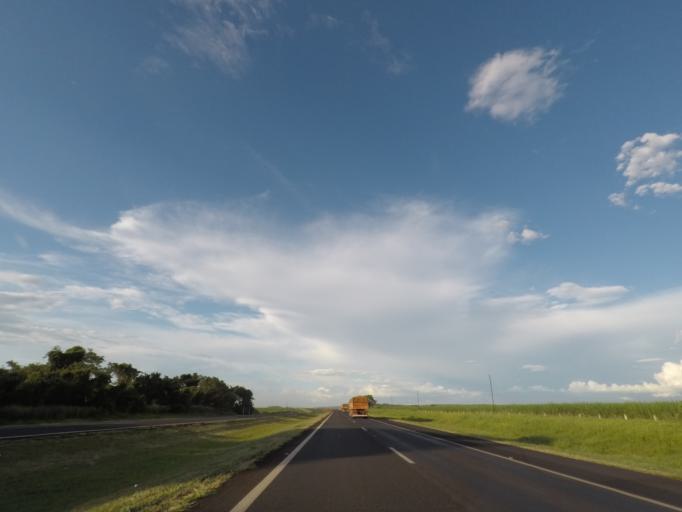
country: BR
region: Sao Paulo
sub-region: Ituverava
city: Ituverava
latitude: -20.3034
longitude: -47.8000
